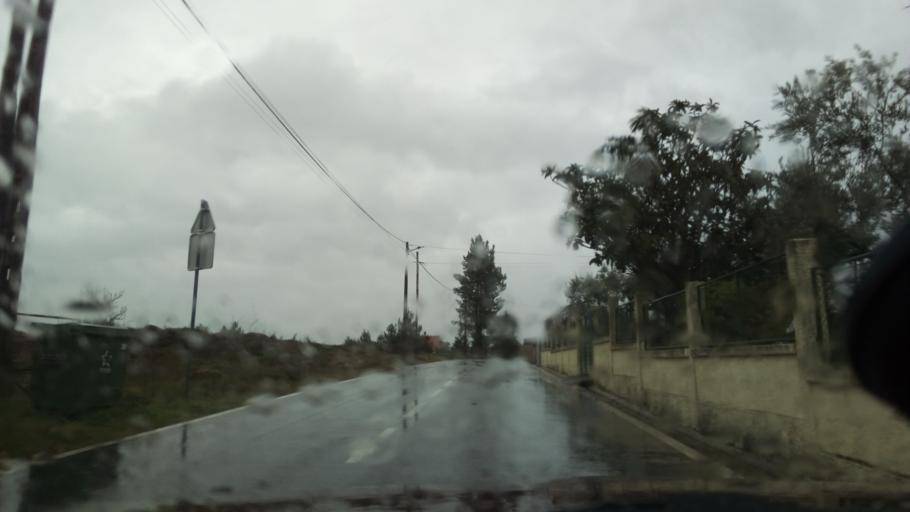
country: PT
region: Guarda
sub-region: Fornos de Algodres
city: Fornos de Algodres
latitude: 40.5546
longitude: -7.5236
